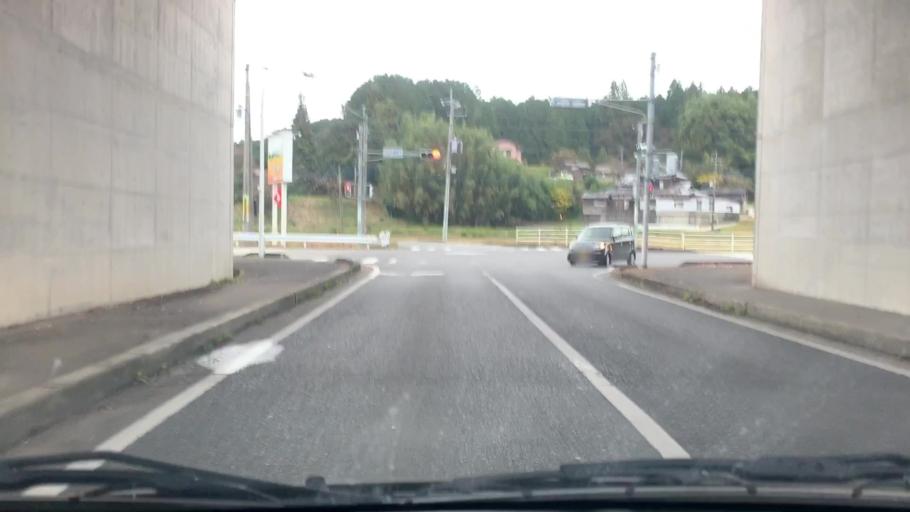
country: JP
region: Saga Prefecture
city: Ureshinomachi-shimojuku
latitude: 33.1263
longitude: 129.9818
